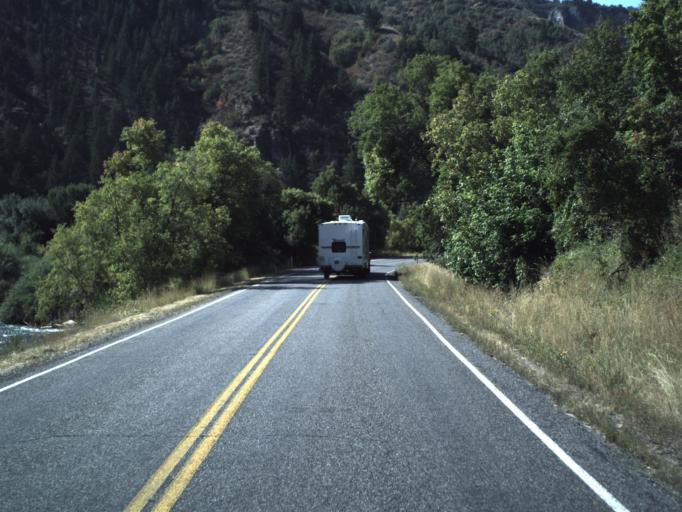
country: US
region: Utah
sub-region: Cache County
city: Millville
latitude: 41.6243
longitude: -111.7316
